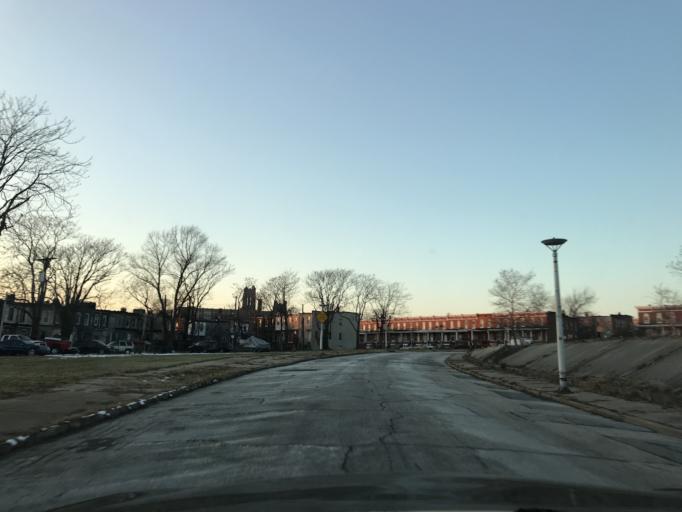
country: US
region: Maryland
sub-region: City of Baltimore
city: Baltimore
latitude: 39.3229
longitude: -76.5913
